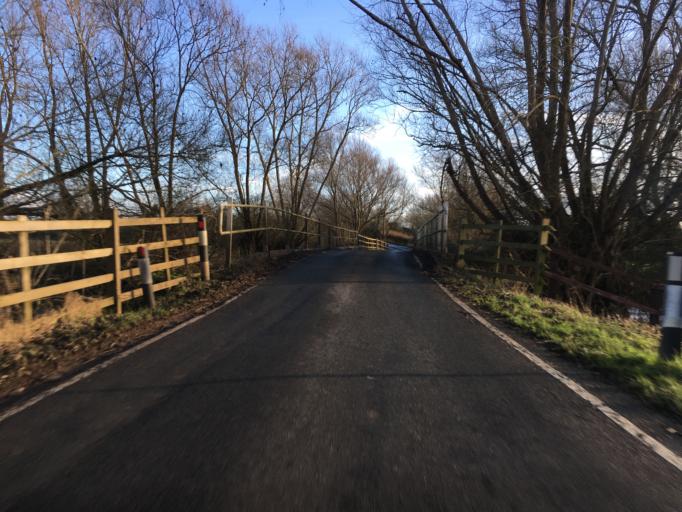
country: GB
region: England
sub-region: Warwickshire
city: Henley in Arden
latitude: 52.2483
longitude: -1.7939
